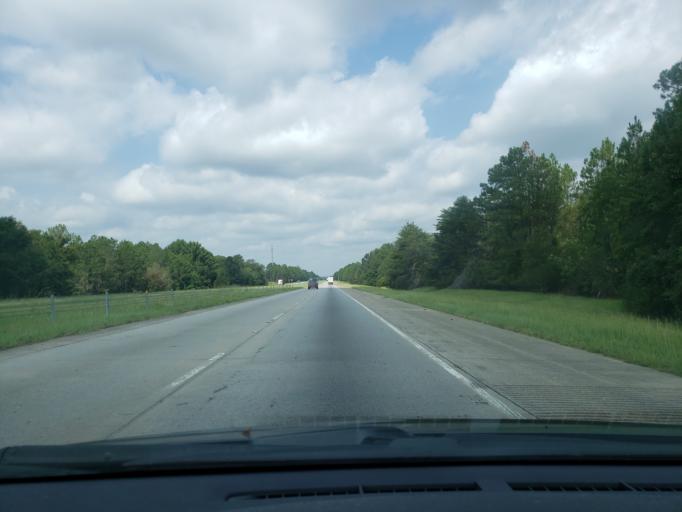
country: US
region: Georgia
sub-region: Treutlen County
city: Soperton
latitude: 32.4252
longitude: -82.4505
